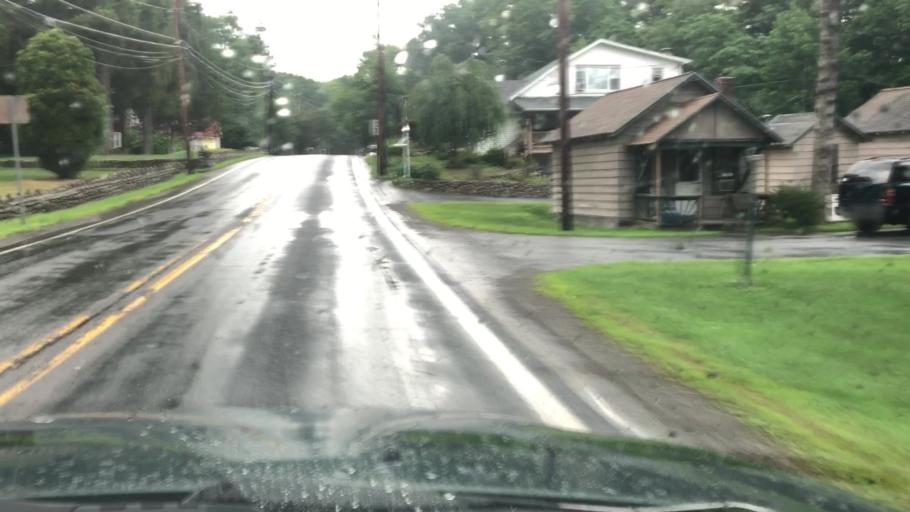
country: US
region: Pennsylvania
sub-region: Monroe County
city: Mountainhome
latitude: 41.1931
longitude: -75.2514
